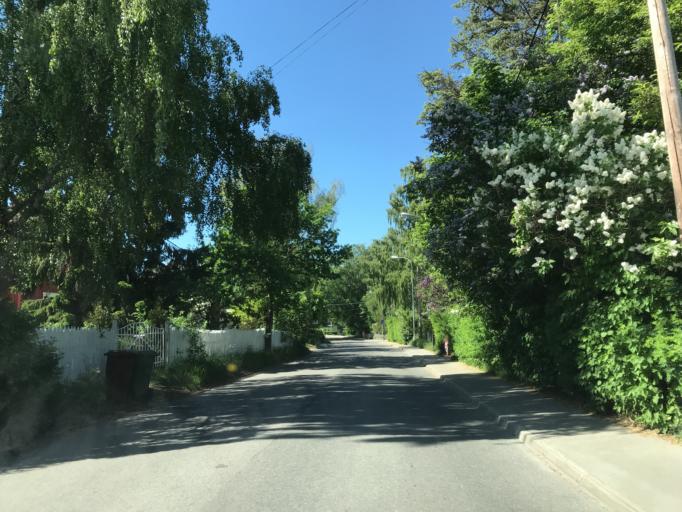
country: SE
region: Stockholm
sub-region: Sollentuna Kommun
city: Sollentuna
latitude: 59.4252
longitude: 17.9618
